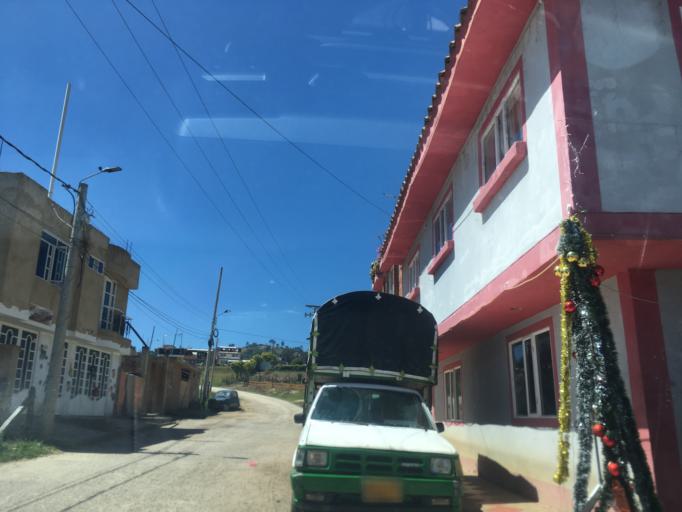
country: CO
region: Boyaca
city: Combita
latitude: 5.6331
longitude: -73.3257
